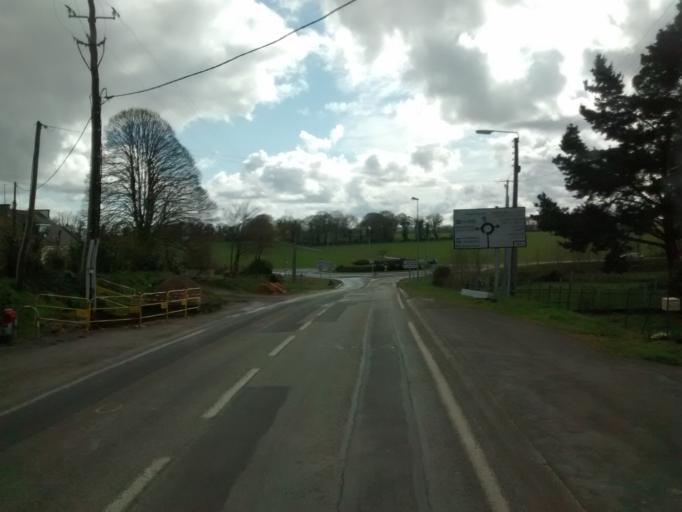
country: FR
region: Brittany
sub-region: Departement du Morbihan
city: Guillac
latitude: 47.8641
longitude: -2.4249
